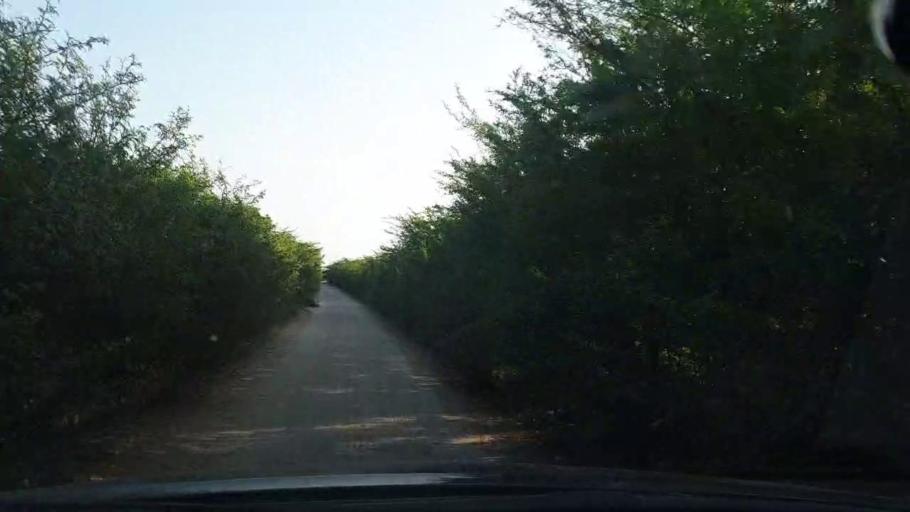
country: PK
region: Sindh
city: Naukot
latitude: 24.7663
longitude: 69.2033
